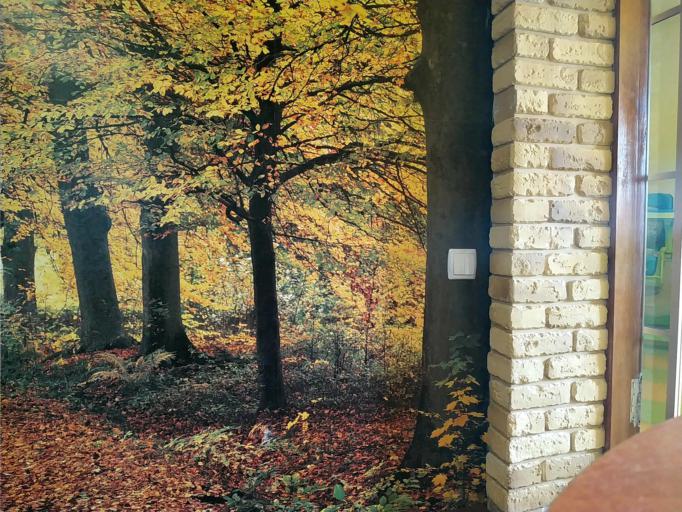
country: RU
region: Smolensk
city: Katyn'
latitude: 54.9094
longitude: 31.7712
